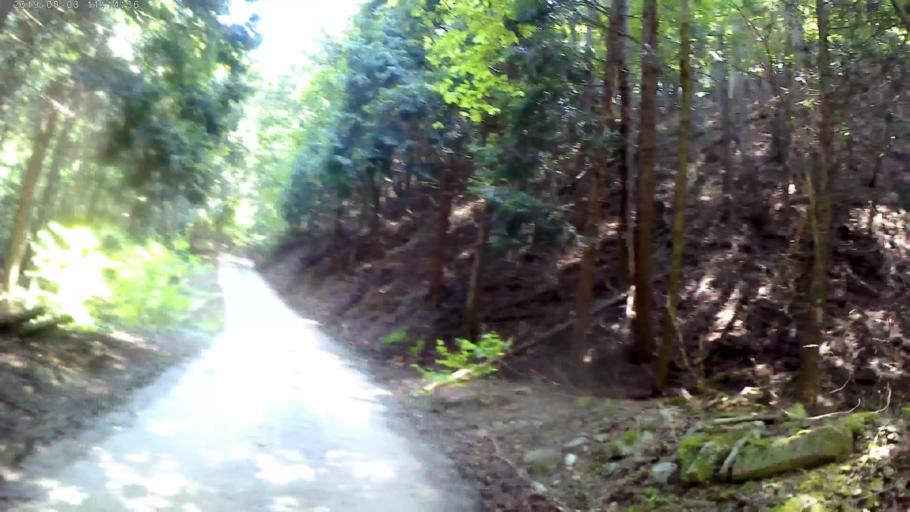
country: JP
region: Yamanashi
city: Enzan
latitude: 35.6148
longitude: 138.7758
